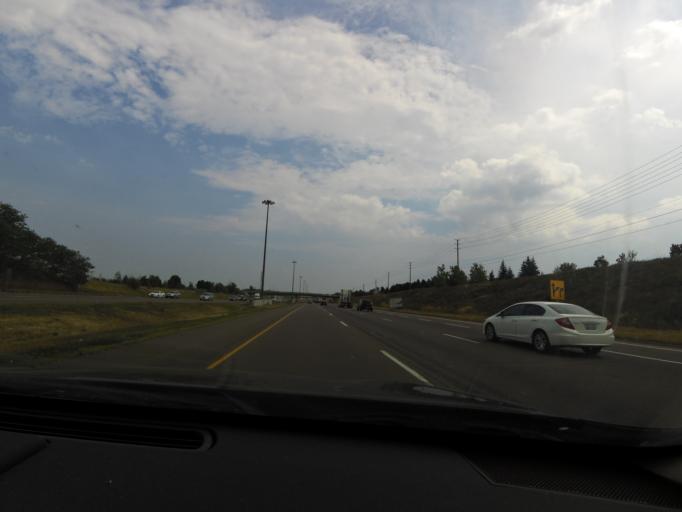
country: CA
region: Ontario
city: Brampton
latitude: 43.7205
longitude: -79.7587
